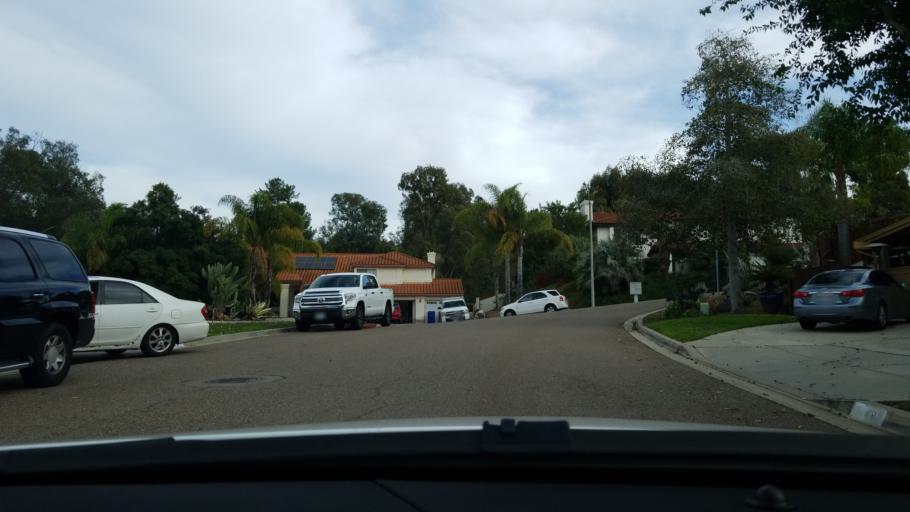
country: US
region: California
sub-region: San Diego County
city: Casa de Oro-Mount Helix
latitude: 32.7740
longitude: -116.9569
